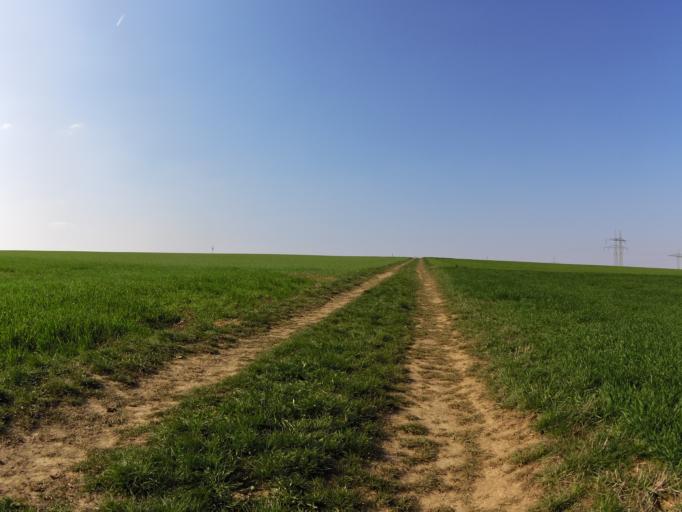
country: DE
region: Bavaria
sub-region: Regierungsbezirk Unterfranken
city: Theilheim
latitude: 49.7623
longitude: 10.0497
